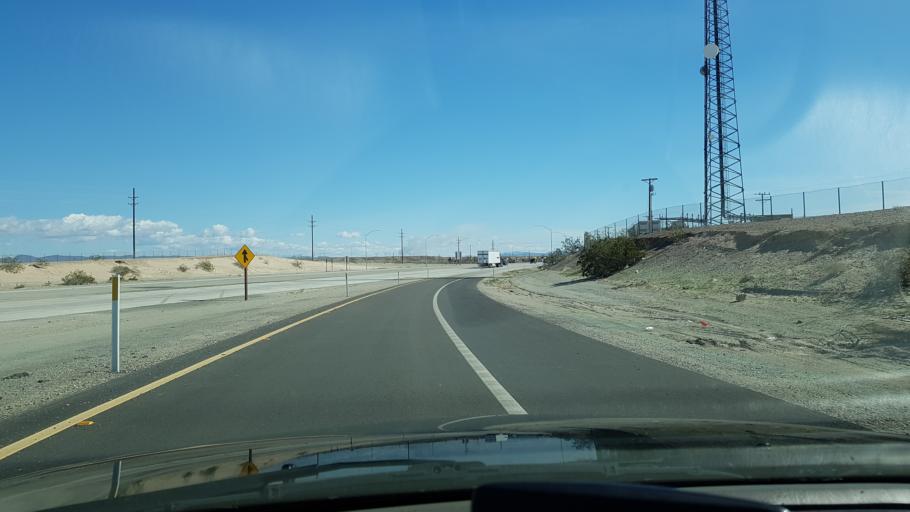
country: MX
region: Baja California
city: Los Algodones
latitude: 32.7464
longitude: -114.7530
